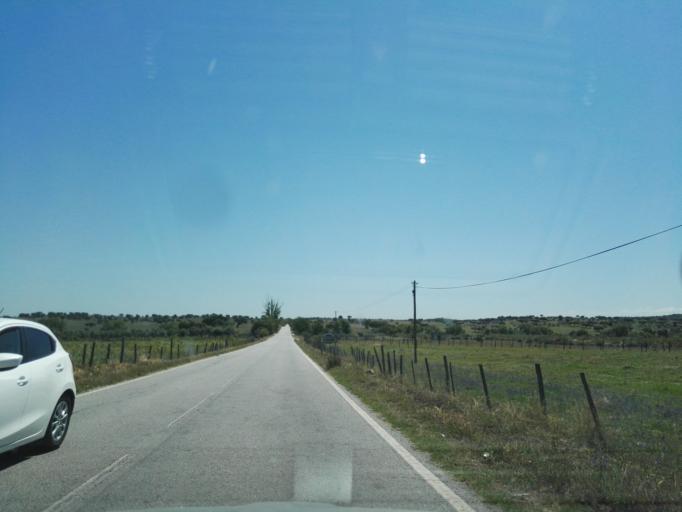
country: PT
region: Portalegre
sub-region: Arronches
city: Arronches
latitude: 39.0101
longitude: -7.2422
